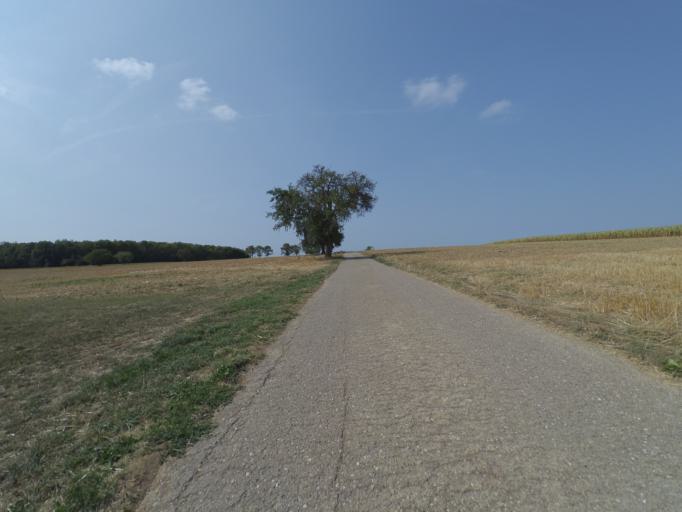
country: DE
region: Rheinland-Pfalz
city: Kirf
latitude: 49.5426
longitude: 6.4444
